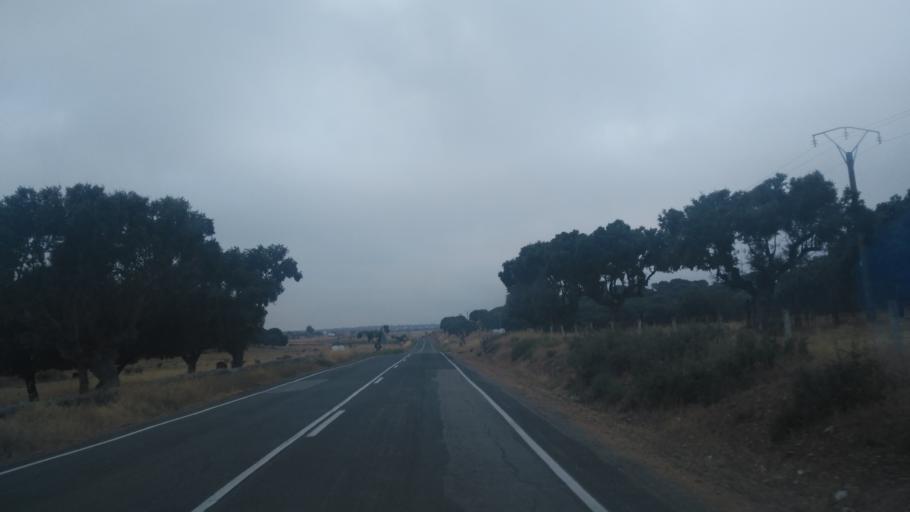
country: ES
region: Castille and Leon
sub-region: Provincia de Salamanca
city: Matilla de los Canos del Rio
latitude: 40.8040
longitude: -5.9240
